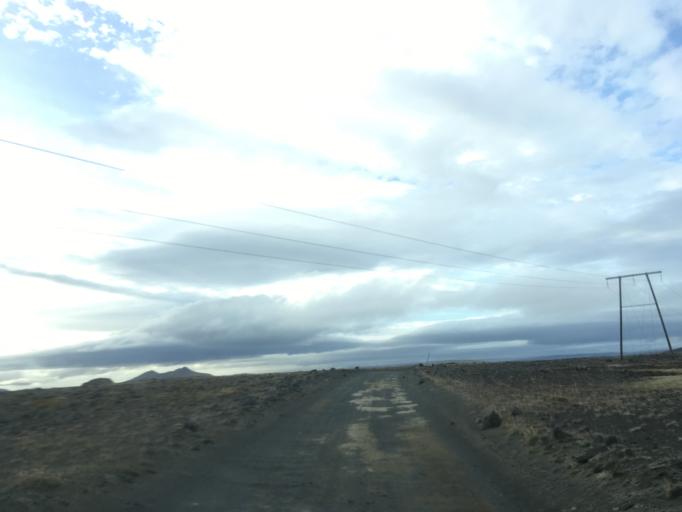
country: IS
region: South
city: Vestmannaeyjar
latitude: 64.1072
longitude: -19.1078
